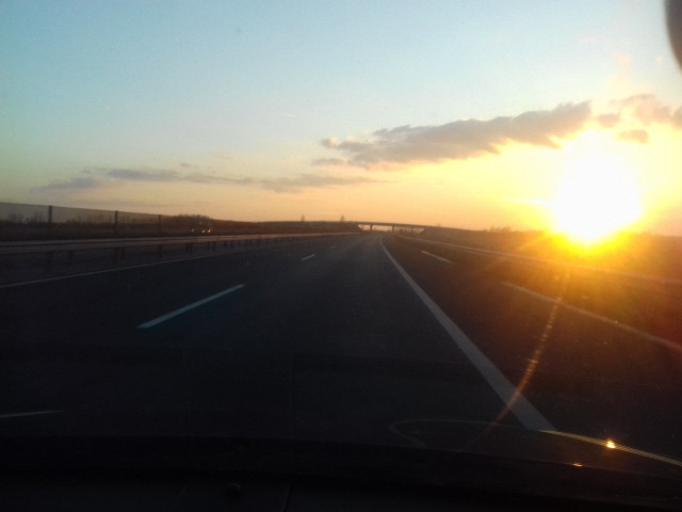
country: HU
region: Hajdu-Bihar
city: Gorbehaza
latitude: 47.8008
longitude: 21.2905
